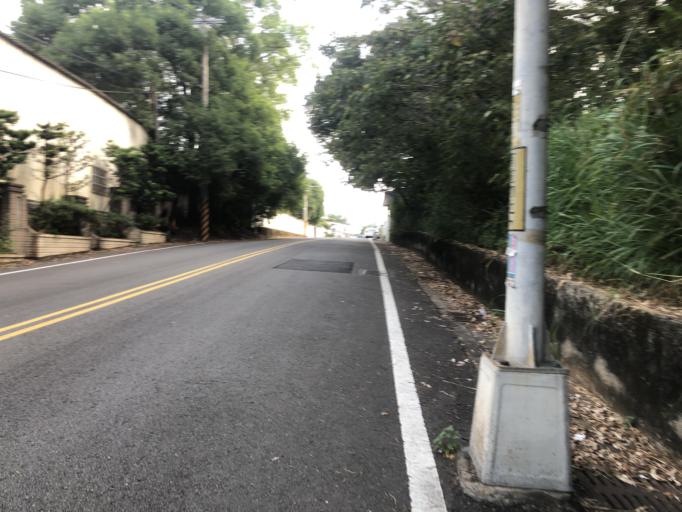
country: TW
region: Taiwan
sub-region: Miaoli
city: Miaoli
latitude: 24.4843
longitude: 120.7931
